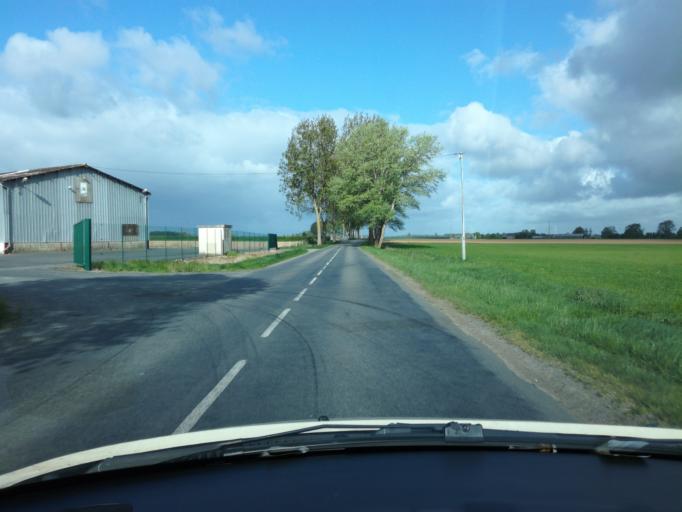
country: FR
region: Picardie
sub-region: Departement de la Somme
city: Hornoy-le-Bourg
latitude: 49.8515
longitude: 1.8860
